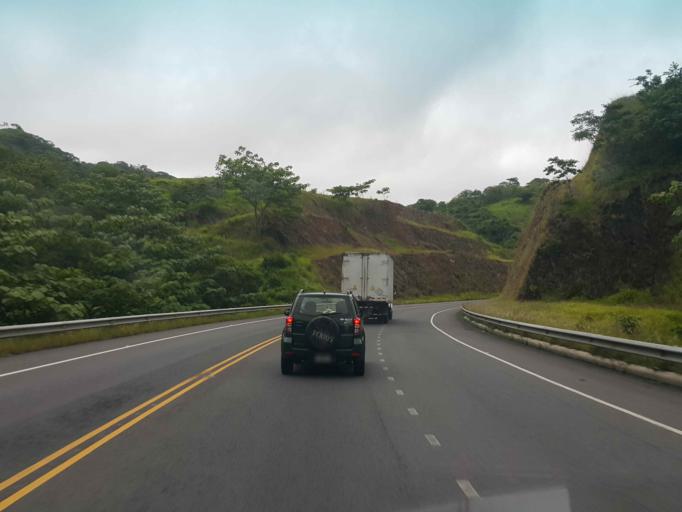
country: CR
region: Alajuela
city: Atenas
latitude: 9.9413
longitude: -84.4003
